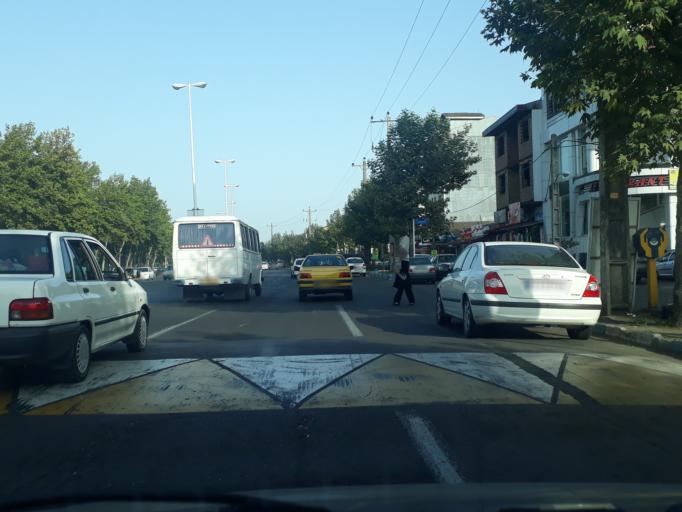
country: IR
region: Gilan
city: Bandar-e Anzali
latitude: 37.4599
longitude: 49.4958
